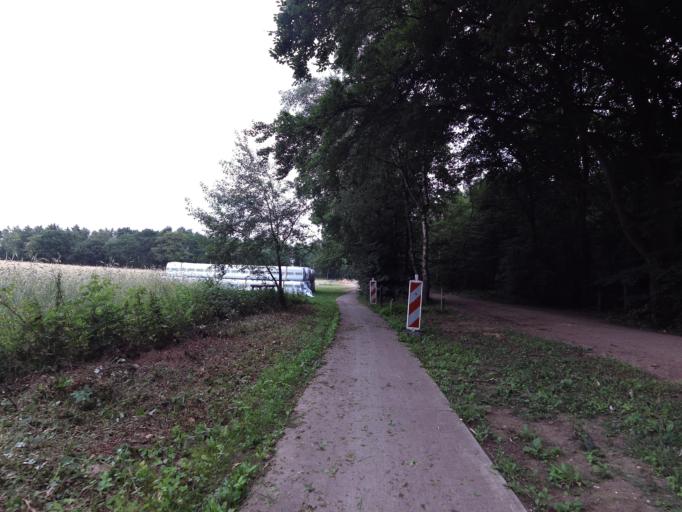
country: NL
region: Gelderland
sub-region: Gemeente Montferland
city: s-Heerenberg
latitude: 51.9002
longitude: 6.2455
